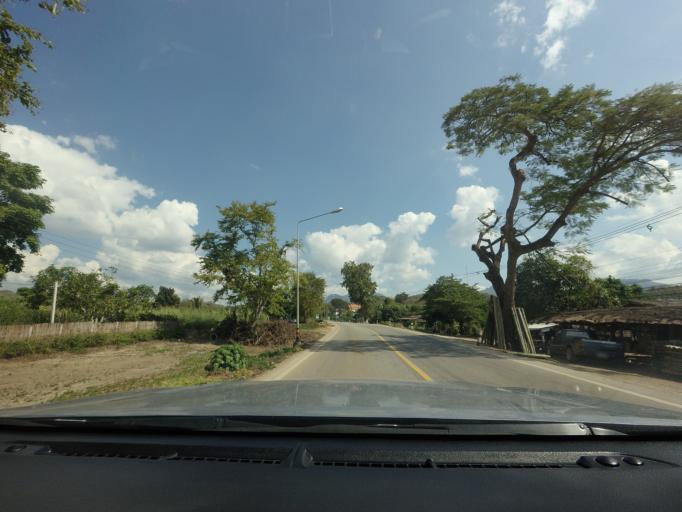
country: TH
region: Chiang Mai
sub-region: Amphoe Chiang Dao
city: Chiang Dao
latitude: 19.4819
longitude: 99.0210
